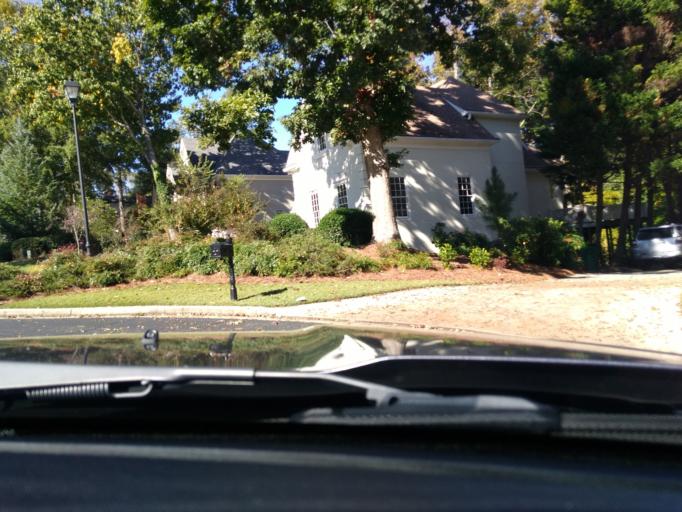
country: US
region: Georgia
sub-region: Fulton County
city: Johns Creek
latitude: 34.0207
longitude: -84.1847
